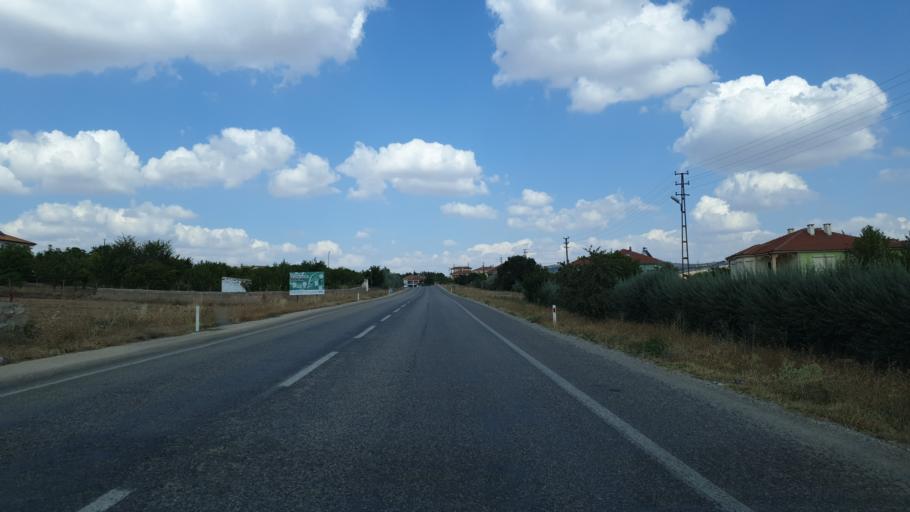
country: TR
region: Kayseri
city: Felahiye
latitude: 39.1044
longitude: 35.5946
